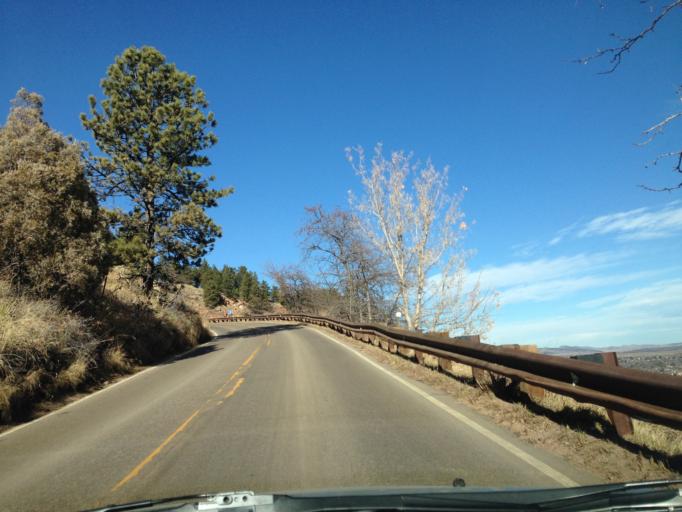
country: US
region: Colorado
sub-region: Boulder County
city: Boulder
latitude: 40.0017
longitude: -105.2912
